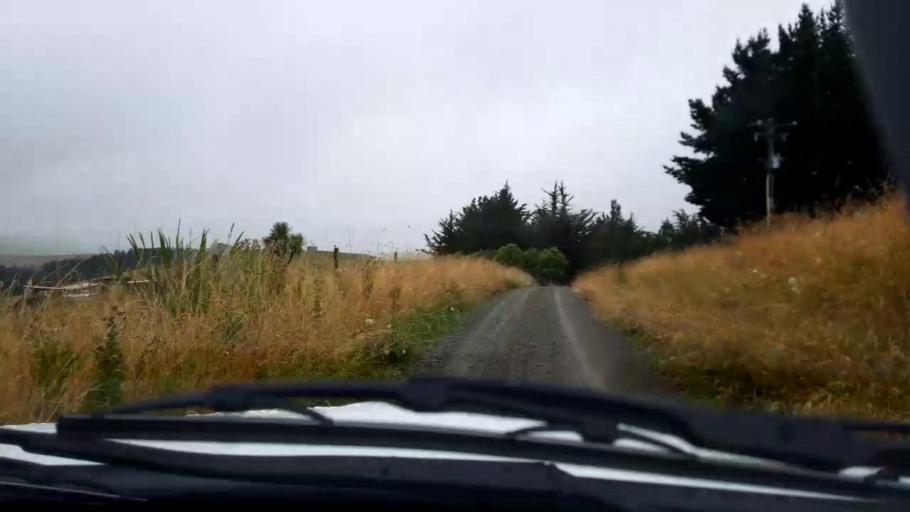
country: NZ
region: Canterbury
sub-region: Timaru District
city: Pleasant Point
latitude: -44.1812
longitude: 171.1023
